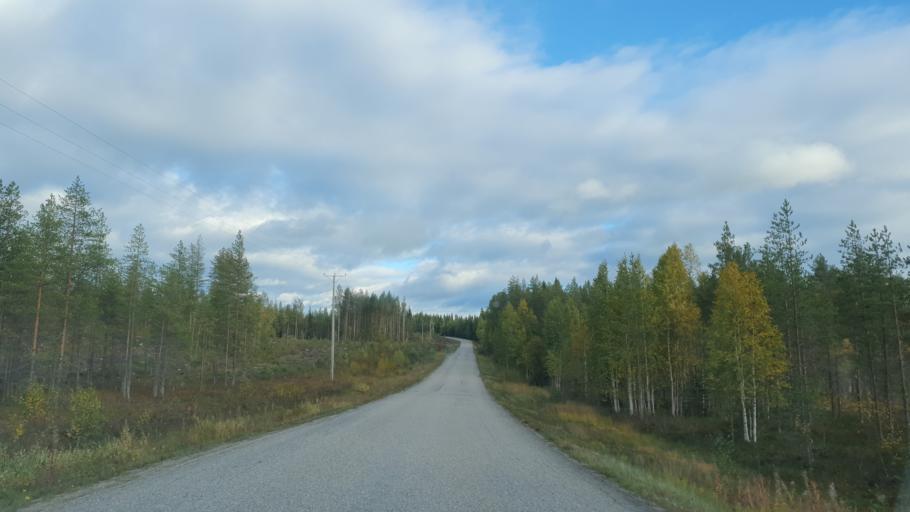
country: FI
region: Kainuu
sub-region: Kehys-Kainuu
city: Kuhmo
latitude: 63.9267
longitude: 30.0080
